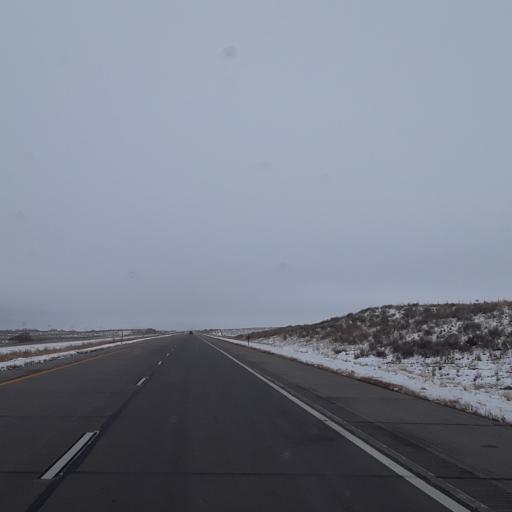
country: US
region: Colorado
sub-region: Logan County
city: Sterling
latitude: 40.5799
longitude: -103.1982
